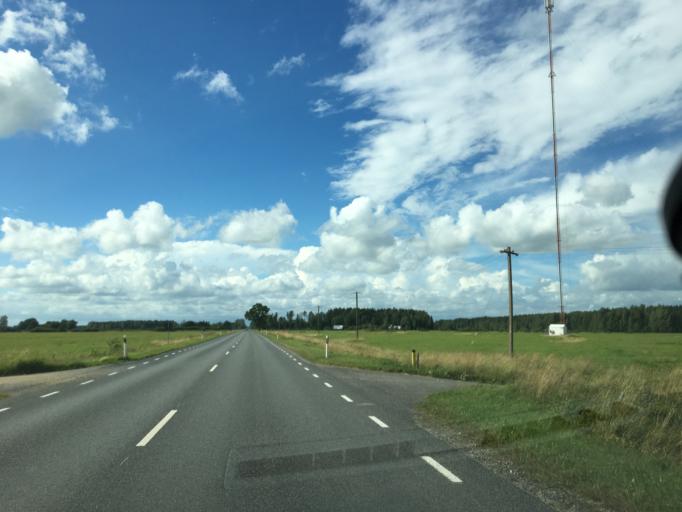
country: EE
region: Paernumaa
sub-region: Vaendra vald (alev)
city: Vandra
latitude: 58.5765
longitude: 25.1935
